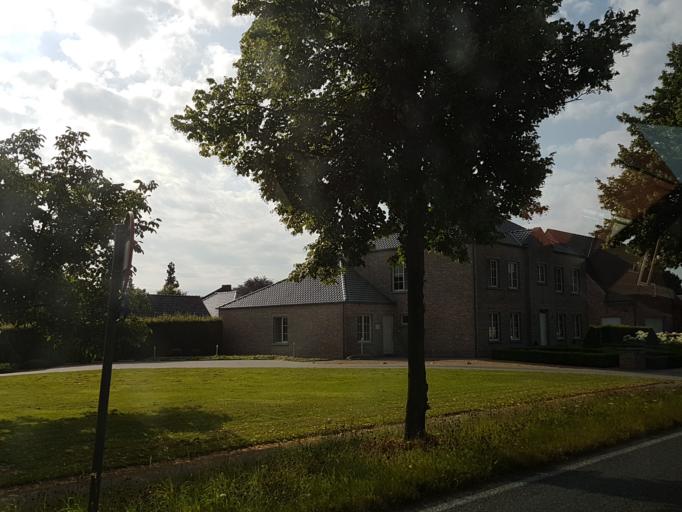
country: BE
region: Flanders
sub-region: Provincie Antwerpen
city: Olen
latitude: 51.1118
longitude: 4.8690
